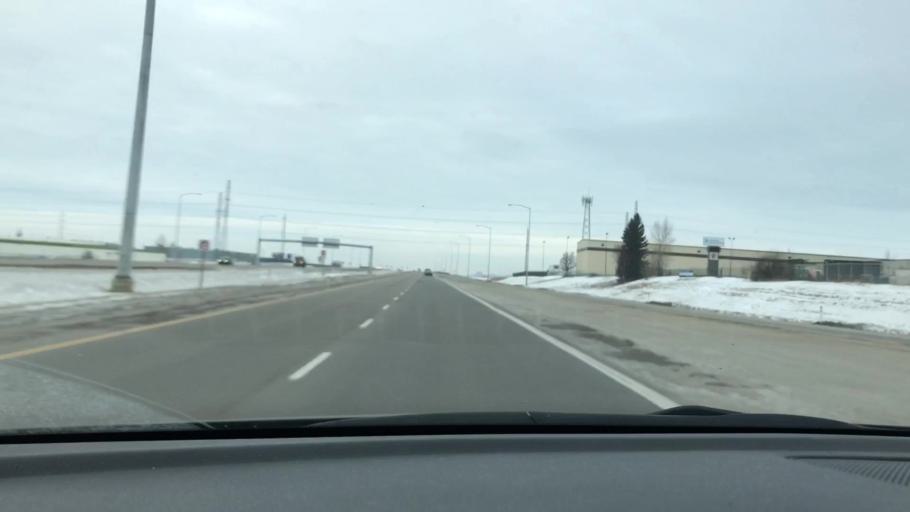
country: CA
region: Alberta
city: Sherwood Park
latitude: 53.5178
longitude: -113.3752
